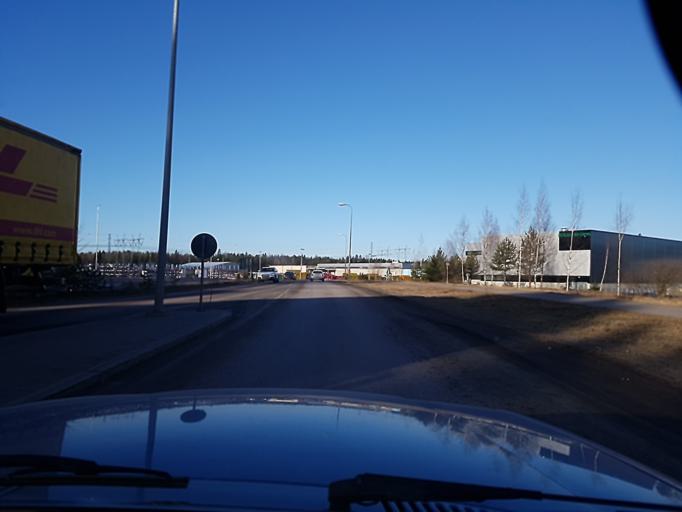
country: FI
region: Uusimaa
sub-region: Helsinki
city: Vantaa
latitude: 60.2945
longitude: 24.9153
